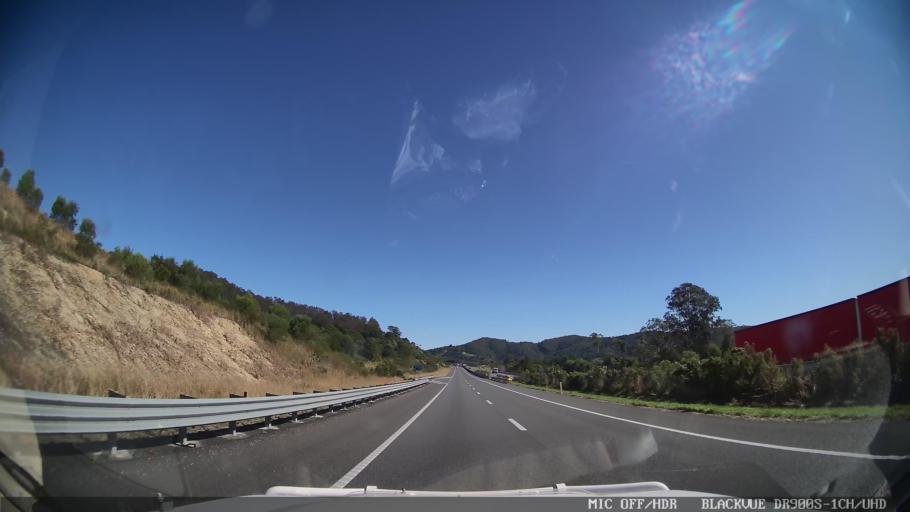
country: AU
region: Queensland
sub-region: Sunshine Coast
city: Black Mountain
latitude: -26.3932
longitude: 152.8152
